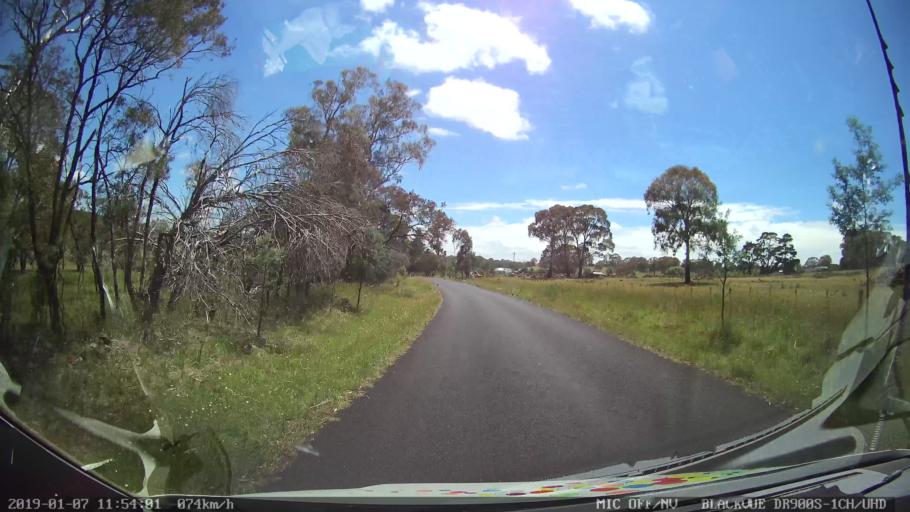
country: AU
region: New South Wales
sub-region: Guyra
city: Guyra
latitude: -30.3006
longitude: 151.6632
